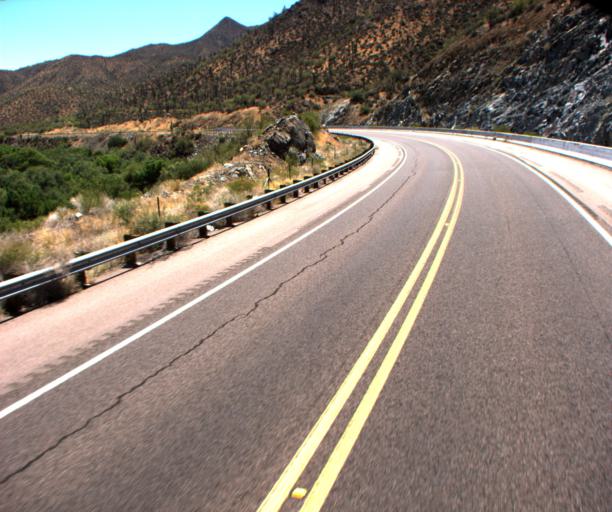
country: US
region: Arizona
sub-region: Pinal County
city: Kearny
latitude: 33.0711
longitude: -110.7253
